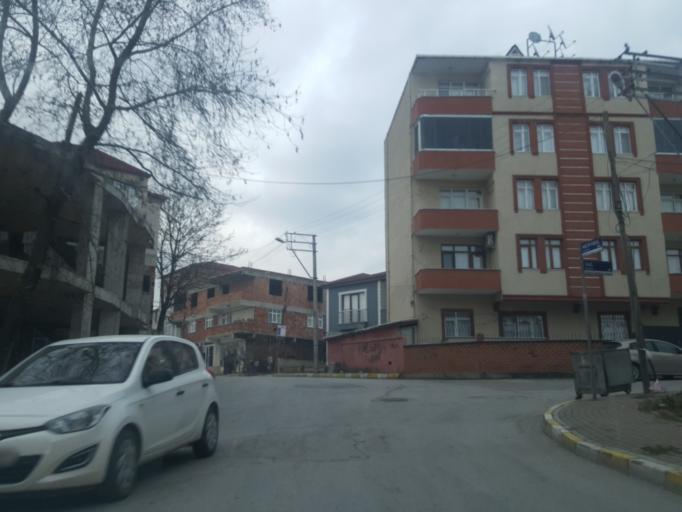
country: TR
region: Kocaeli
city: Tavsancil
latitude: 40.7890
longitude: 29.5444
